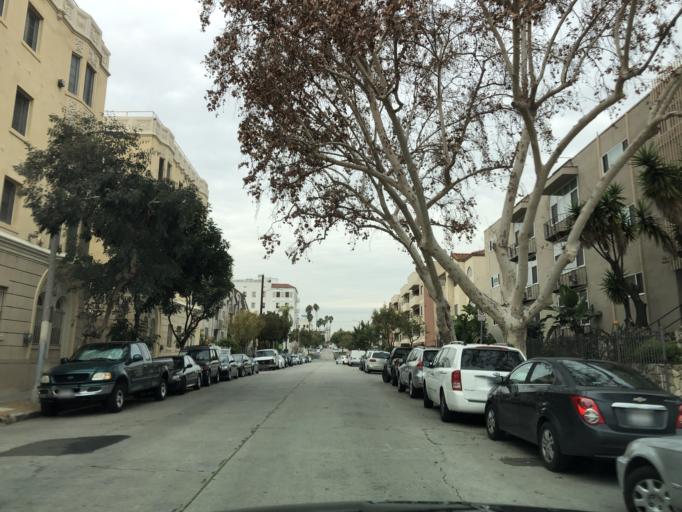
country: US
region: California
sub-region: Los Angeles County
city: Hollywood
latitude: 34.0563
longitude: -118.3122
